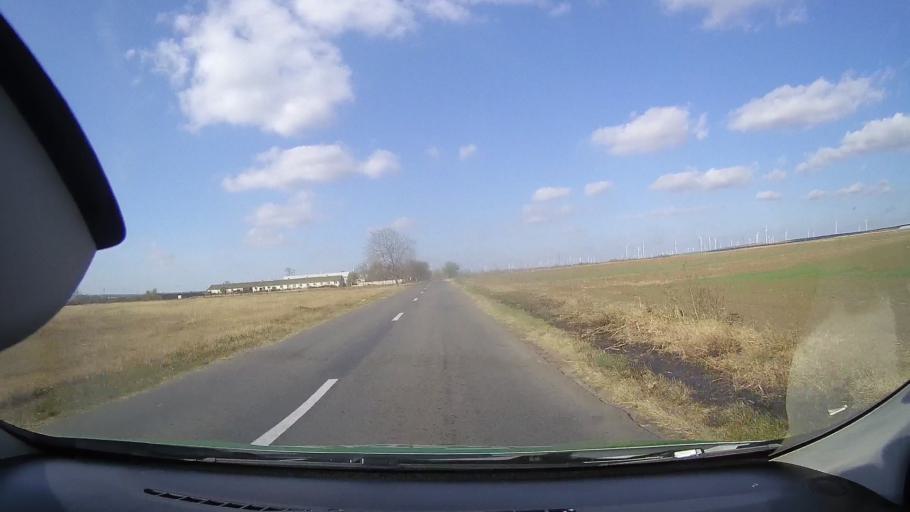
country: RO
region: Constanta
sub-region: Comuna Cogealac
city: Tariverde
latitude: 44.5602
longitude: 28.6096
